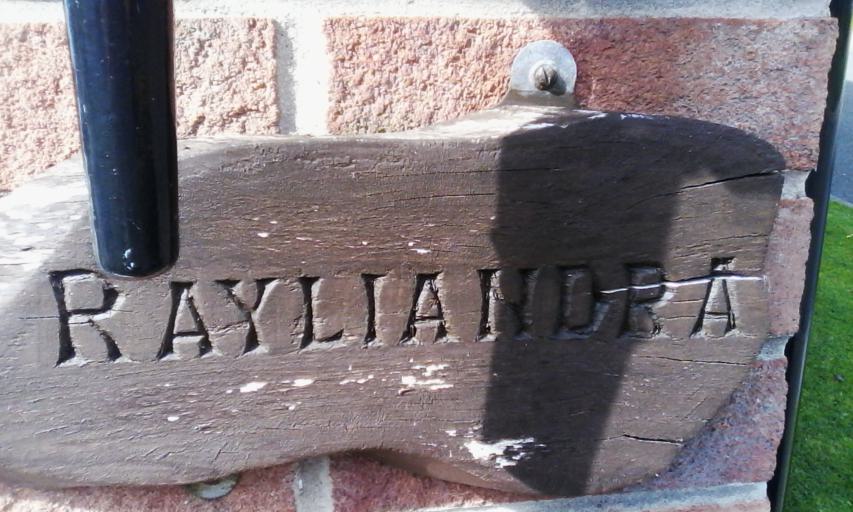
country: GB
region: England
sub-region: Nottinghamshire
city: Arnold
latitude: 52.9776
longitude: -1.0971
